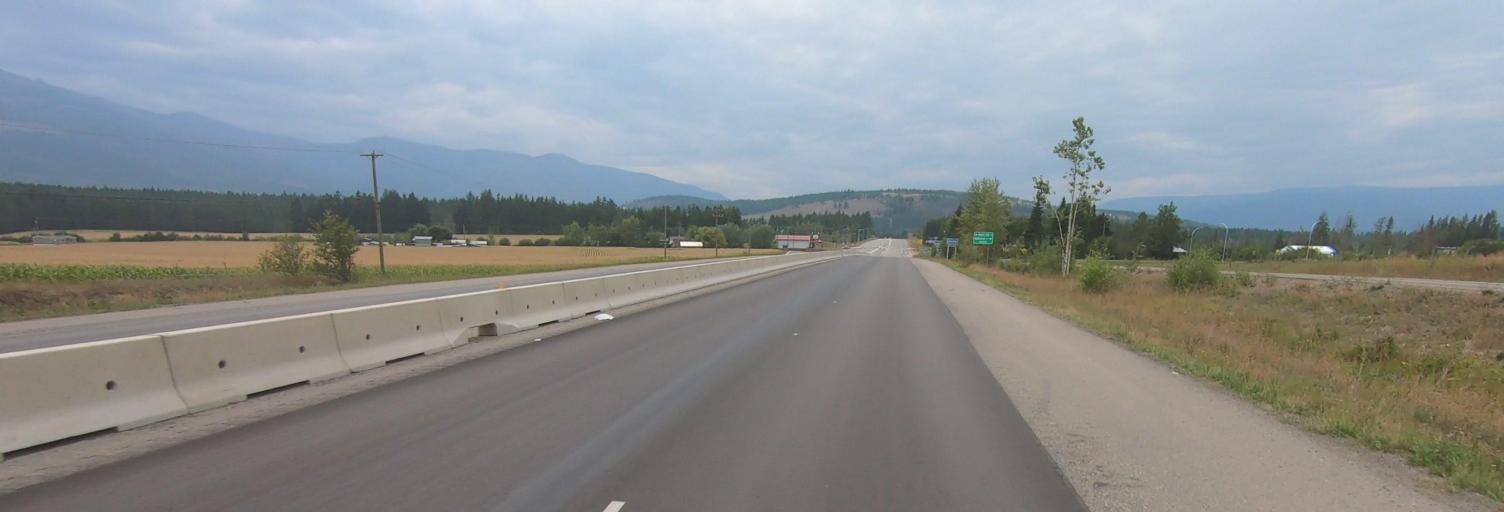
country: CA
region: British Columbia
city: Salmon Arm
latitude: 50.8510
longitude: -119.3484
